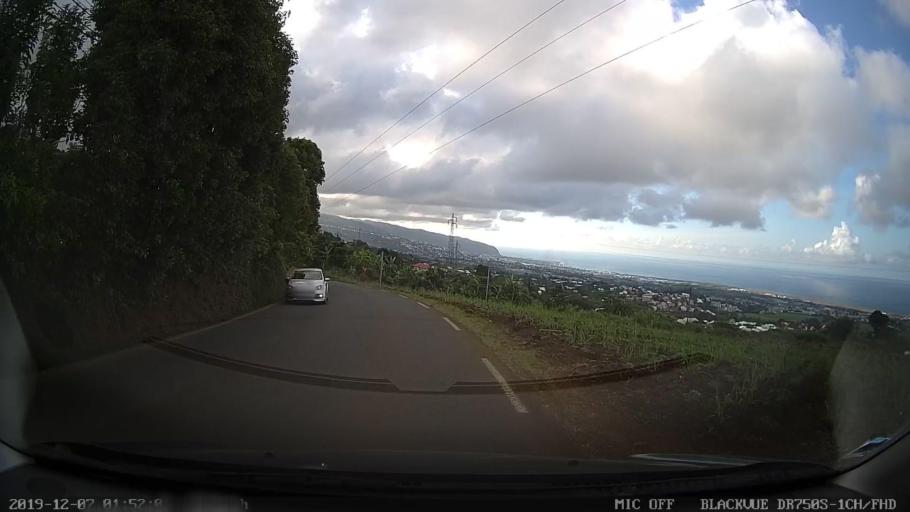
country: RE
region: Reunion
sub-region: Reunion
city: Sainte-Marie
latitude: -20.9411
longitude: 55.5346
